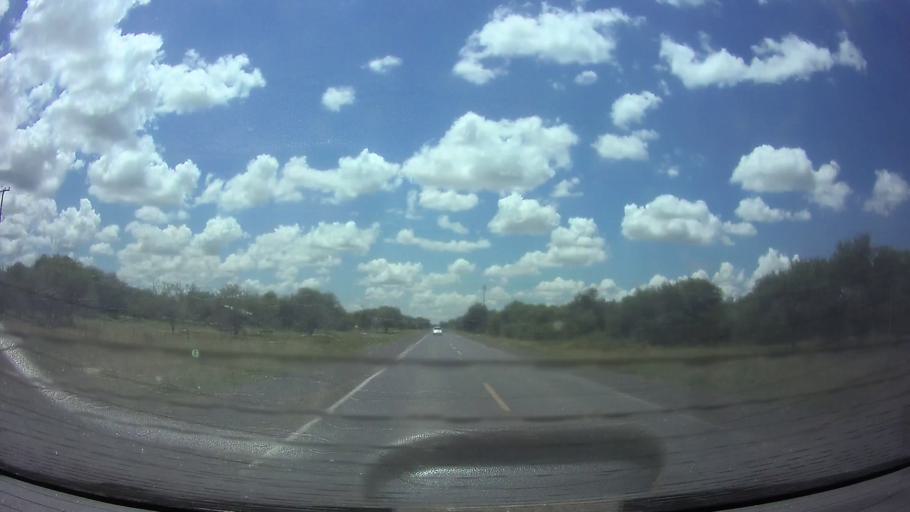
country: PY
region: Presidente Hayes
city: Nanawa
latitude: -25.2271
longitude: -57.6872
